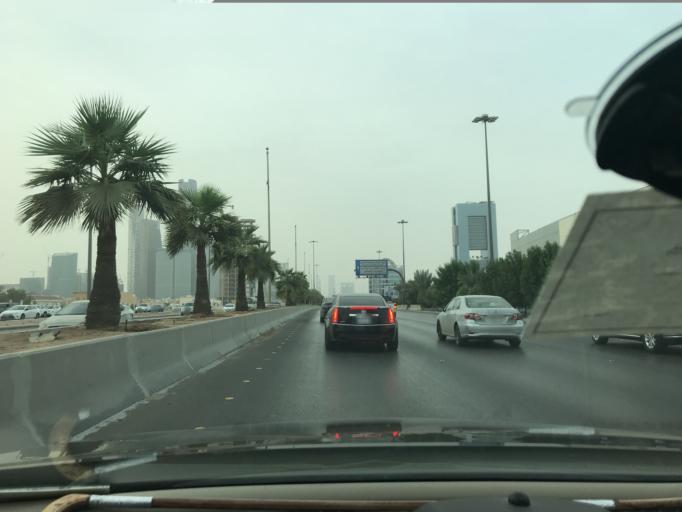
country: SA
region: Ar Riyad
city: Riyadh
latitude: 24.7511
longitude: 46.6523
